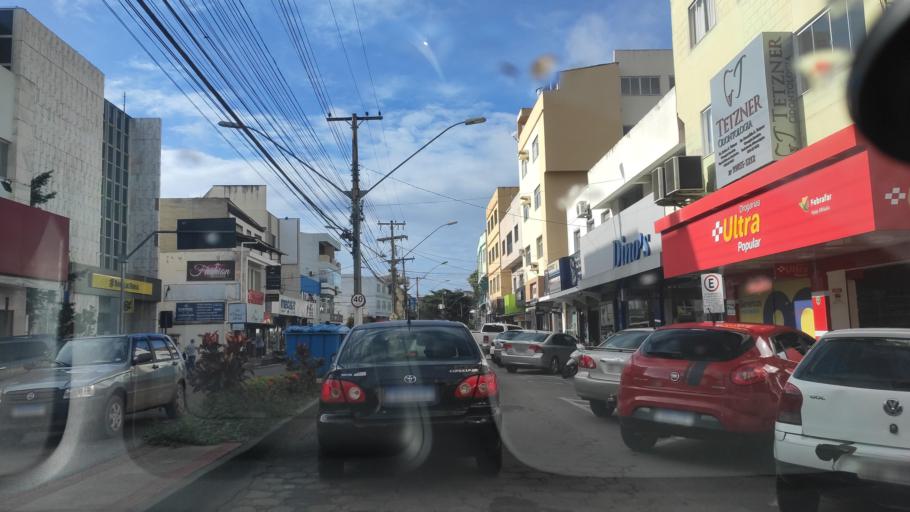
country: BR
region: Espirito Santo
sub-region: Nova Venecia
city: Nova Venecia
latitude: -18.7105
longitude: -40.3990
